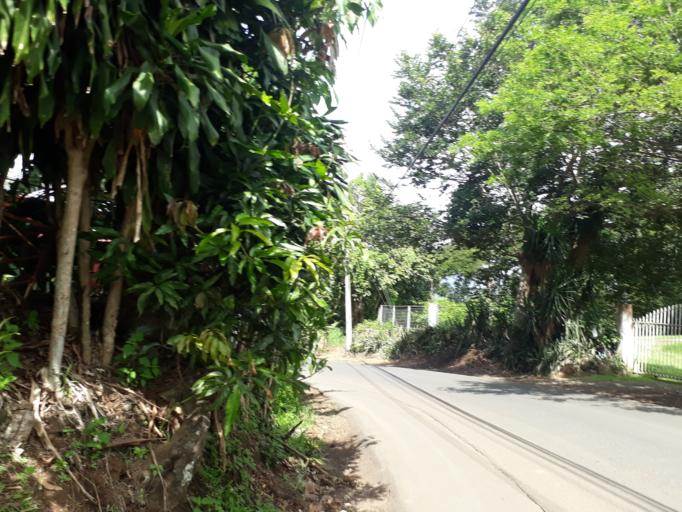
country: CR
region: Alajuela
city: Atenas
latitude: 10.0221
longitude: -84.3404
